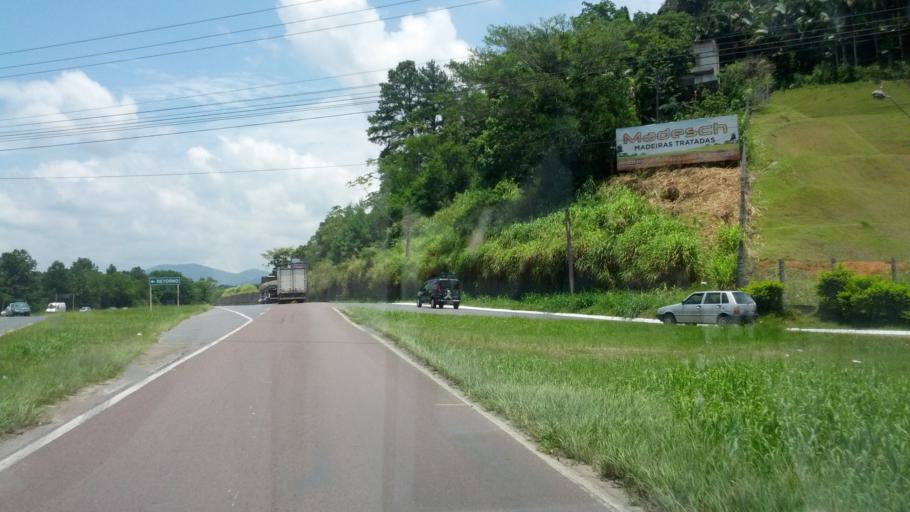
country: BR
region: Santa Catarina
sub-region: Blumenau
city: Blumenau
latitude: -26.8649
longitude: -49.0992
